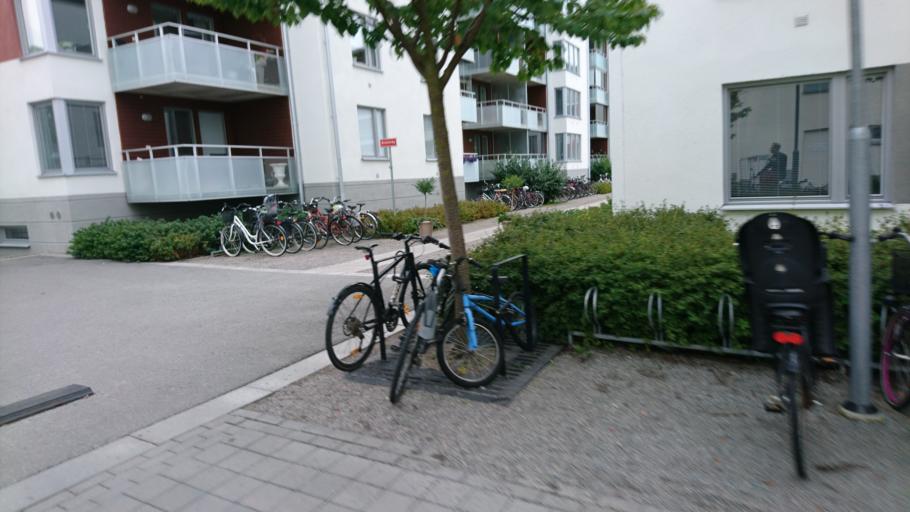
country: SE
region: Uppsala
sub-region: Uppsala Kommun
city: Uppsala
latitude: 59.8676
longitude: 17.6232
